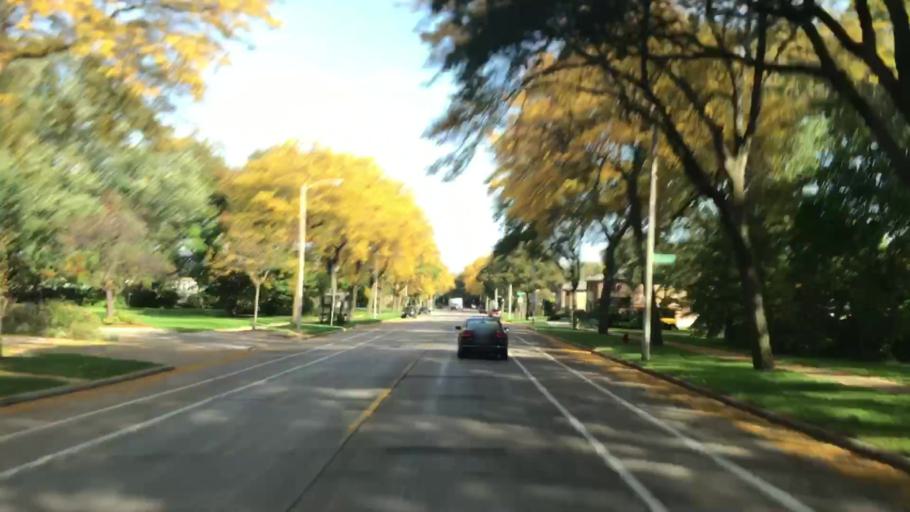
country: US
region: Wisconsin
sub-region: Milwaukee County
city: Shorewood
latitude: 43.0836
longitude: -87.8975
